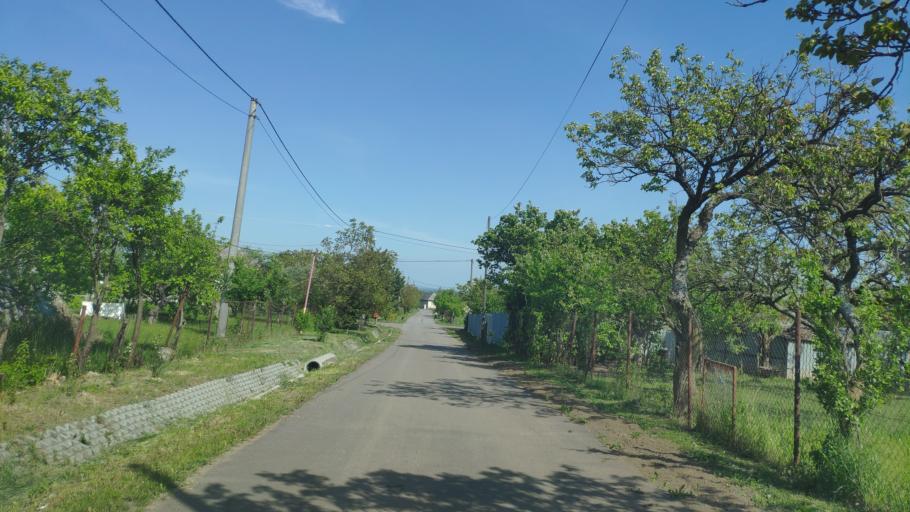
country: SK
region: Kosicky
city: Secovce
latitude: 48.6838
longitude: 21.6103
